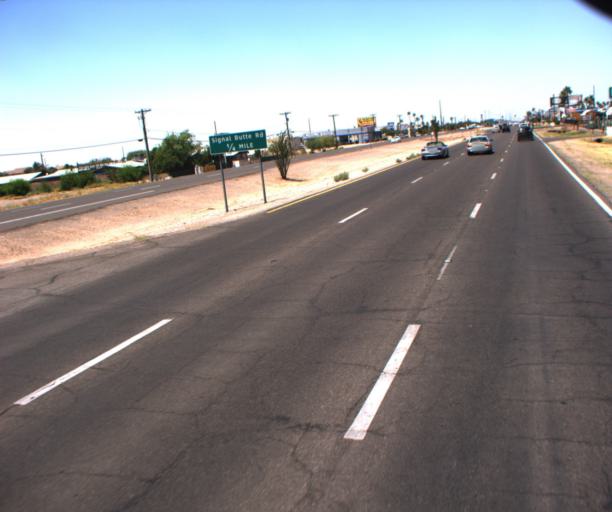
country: US
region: Arizona
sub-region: Pinal County
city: Apache Junction
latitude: 33.4154
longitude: -111.5933
